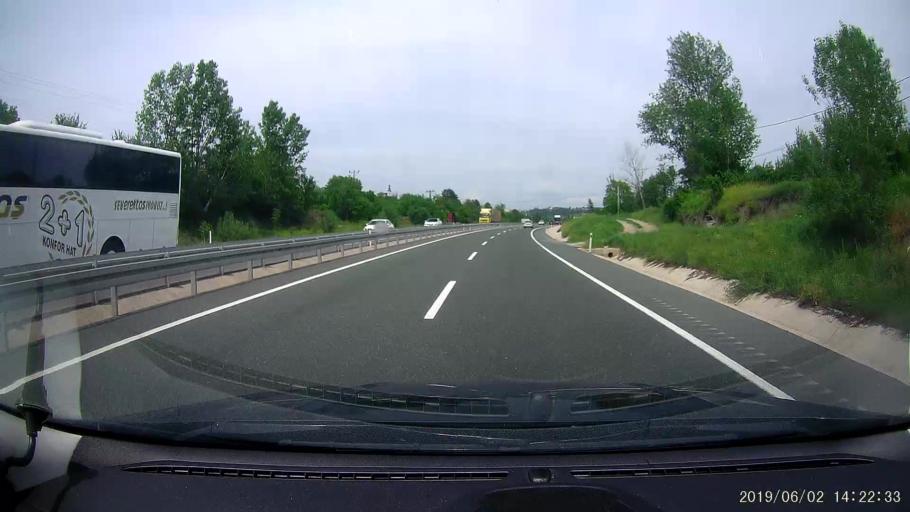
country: TR
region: Kastamonu
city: Tosya
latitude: 40.9956
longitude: 34.0183
